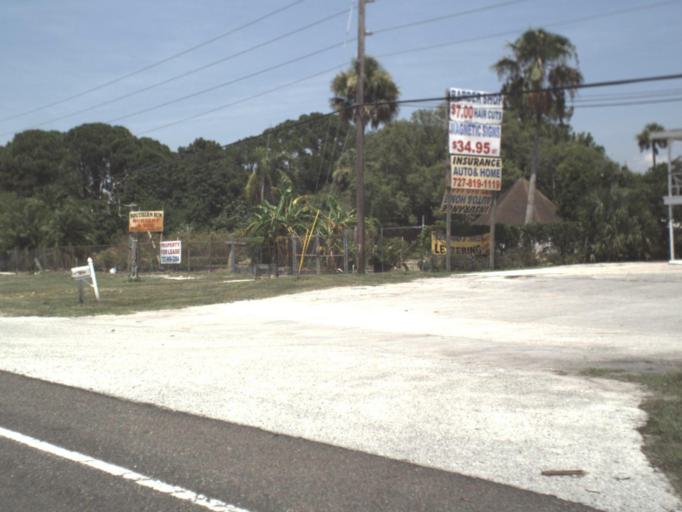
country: US
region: Florida
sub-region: Pasco County
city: Hudson
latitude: 28.3587
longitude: -82.6974
